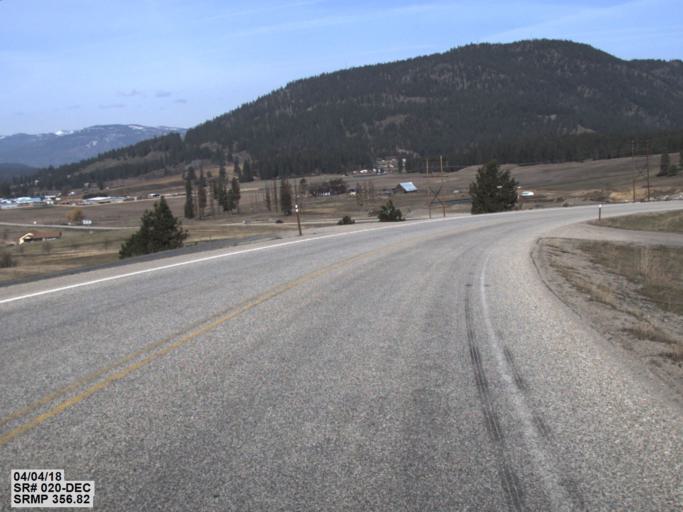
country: US
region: Washington
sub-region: Stevens County
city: Colville
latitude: 48.5447
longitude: -117.8541
